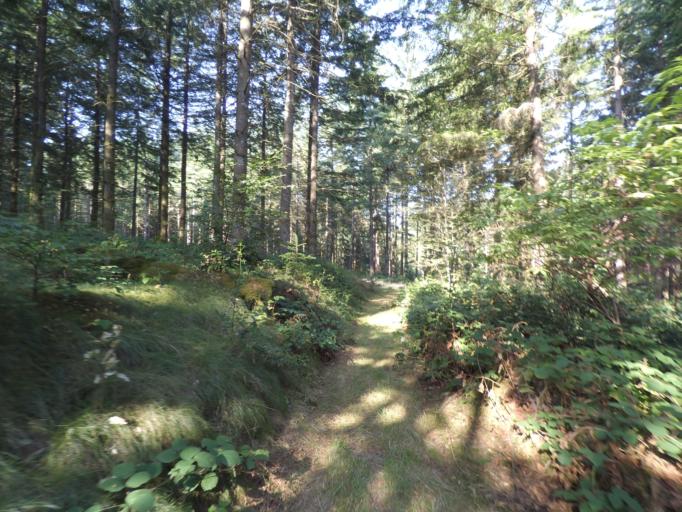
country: FR
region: Limousin
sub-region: Departement de la Correze
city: Bugeat
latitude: 45.6801
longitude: 2.0193
